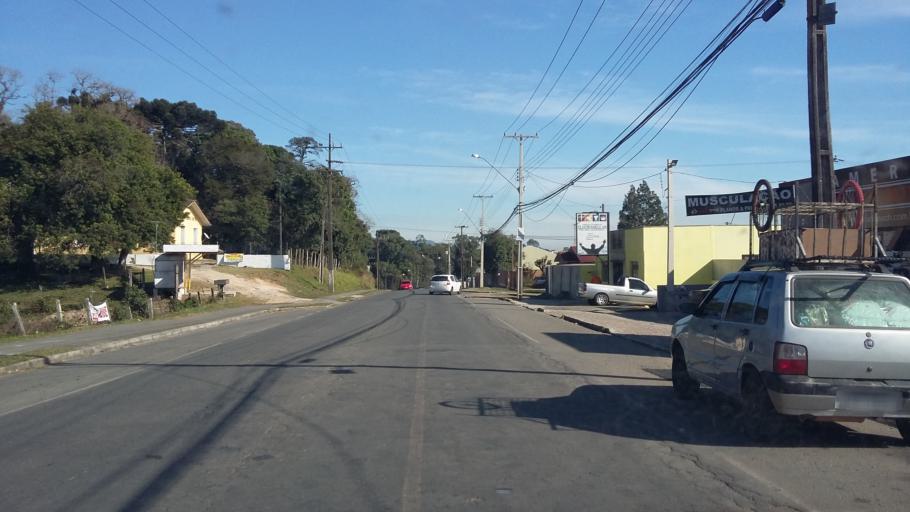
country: BR
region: Parana
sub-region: Campo Largo
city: Campo Largo
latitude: -25.4586
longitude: -49.5488
